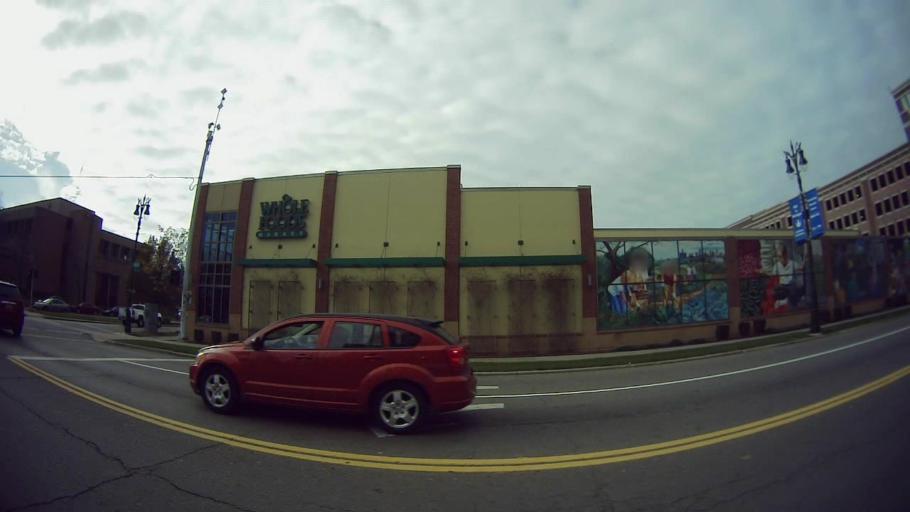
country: US
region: Michigan
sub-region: Wayne County
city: Detroit
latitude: 42.3487
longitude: -83.0560
